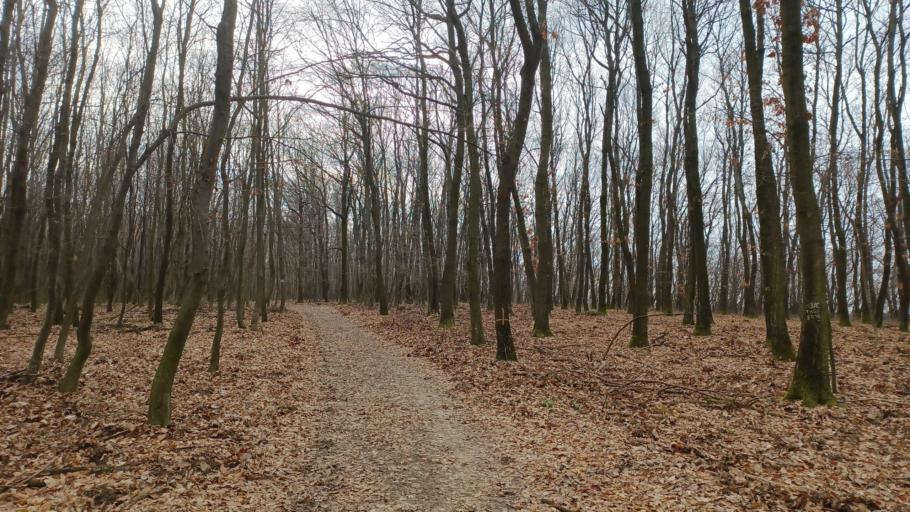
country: HU
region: Tolna
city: Szentgalpuszta
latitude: 46.3292
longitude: 18.6376
